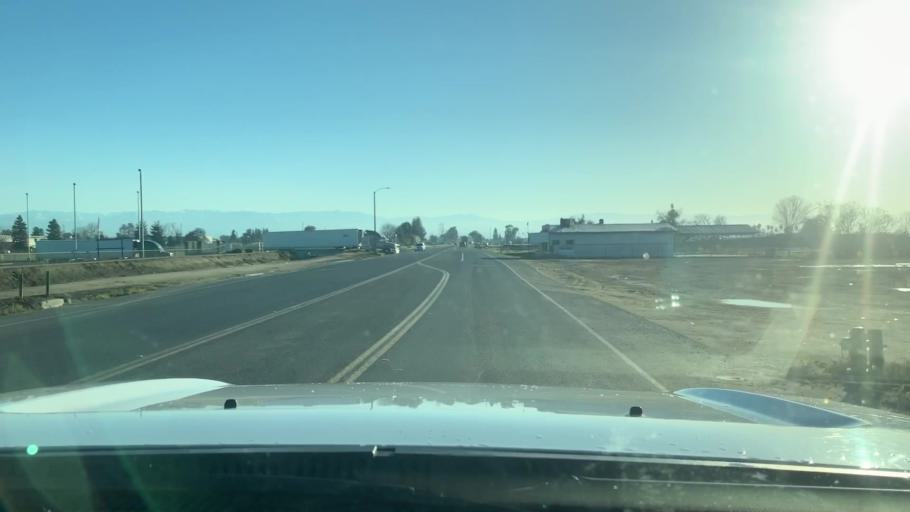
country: US
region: California
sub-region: Tulare County
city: Tulare
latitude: 36.1821
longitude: -119.3378
